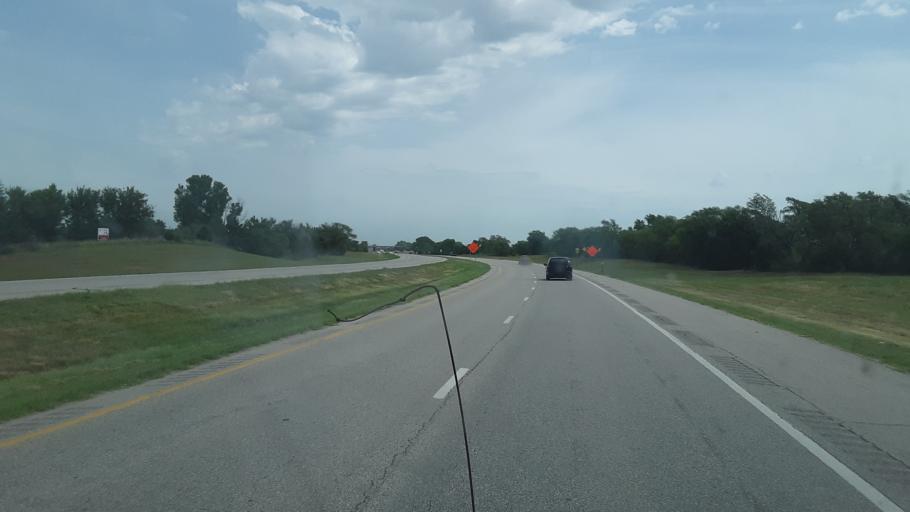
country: US
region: Kansas
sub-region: Sedgwick County
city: Kechi
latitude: 37.7710
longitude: -97.2954
